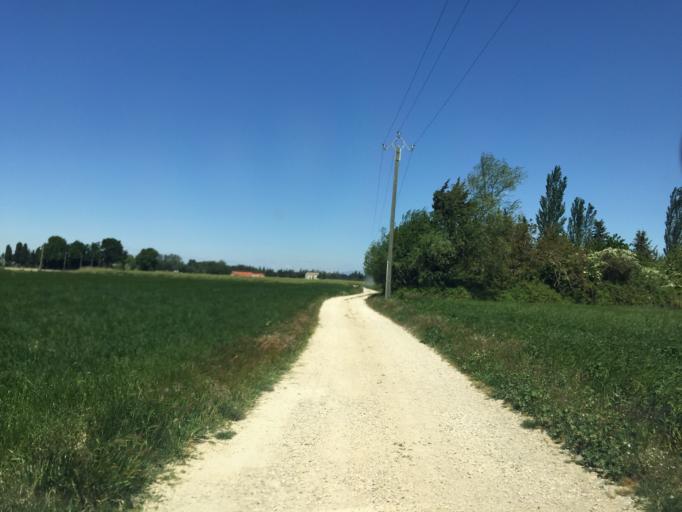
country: FR
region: Provence-Alpes-Cote d'Azur
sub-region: Departement du Vaucluse
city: Bedarrides
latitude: 44.0654
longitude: 4.9021
